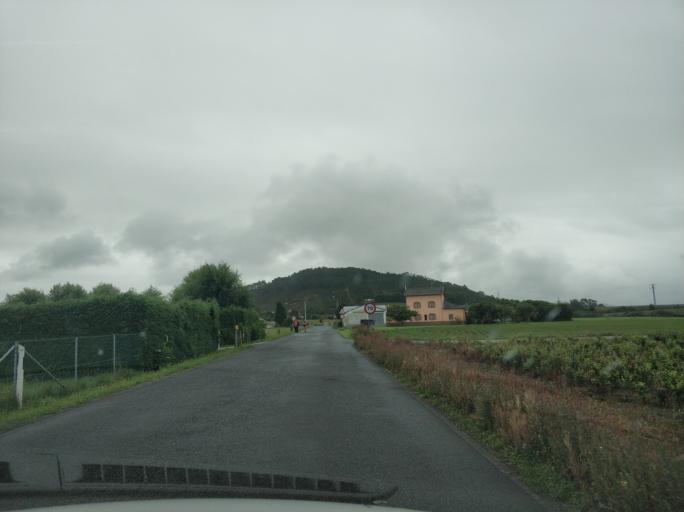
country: ES
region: Asturias
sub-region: Province of Asturias
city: Tineo
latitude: 43.5488
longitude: -6.4493
